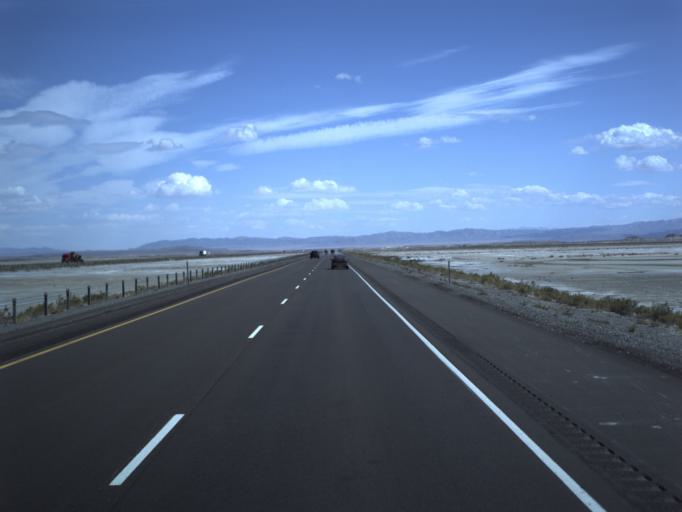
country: US
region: Utah
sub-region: Tooele County
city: Wendover
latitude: 40.7276
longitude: -113.3319
